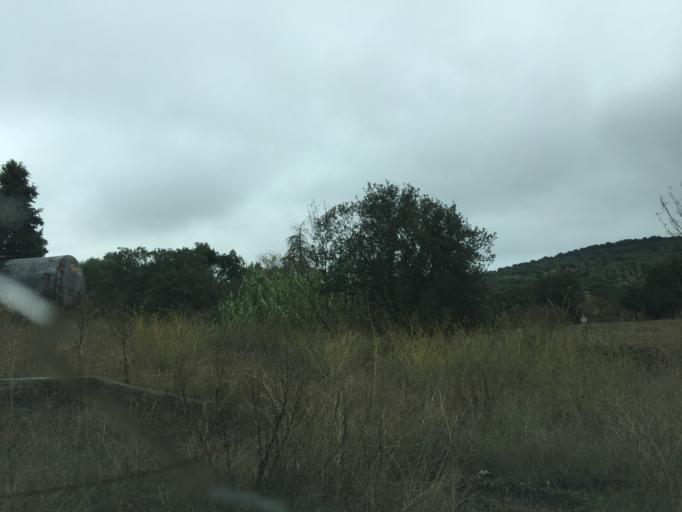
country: PT
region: Portalegre
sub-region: Alter do Chao
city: Alter do Chao
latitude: 39.2249
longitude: -7.6535
